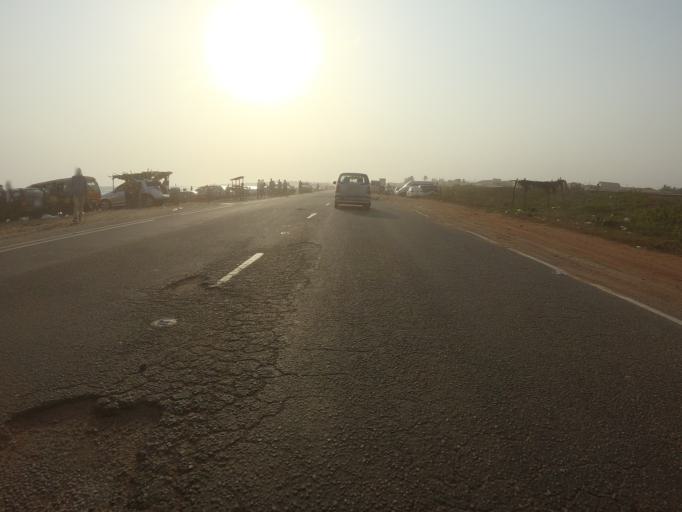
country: GH
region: Greater Accra
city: Nungua
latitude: 5.6122
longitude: -0.0426
